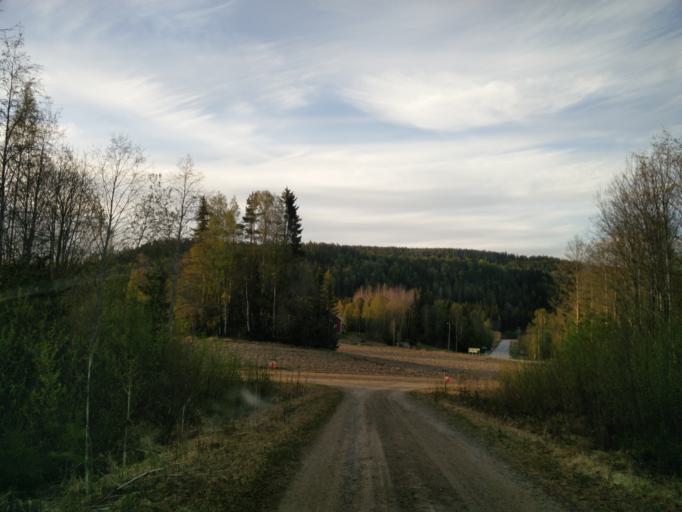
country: SE
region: Vaesternorrland
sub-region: Sundsvalls Kommun
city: Matfors
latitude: 62.4026
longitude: 16.8268
